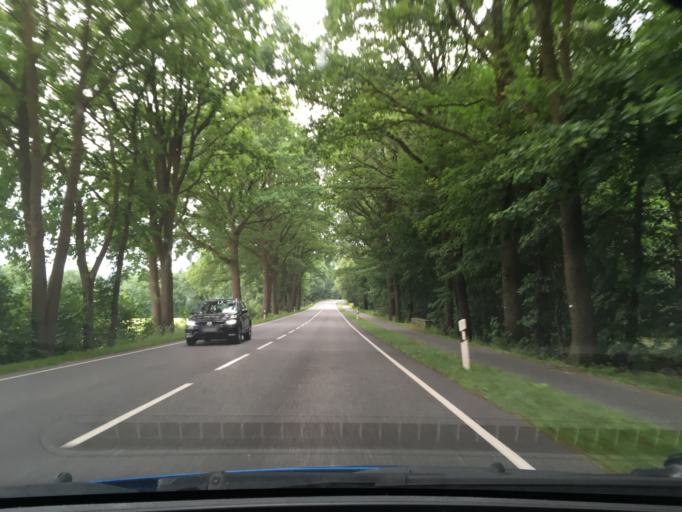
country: DE
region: Lower Saxony
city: Appel
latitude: 53.3974
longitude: 9.7906
